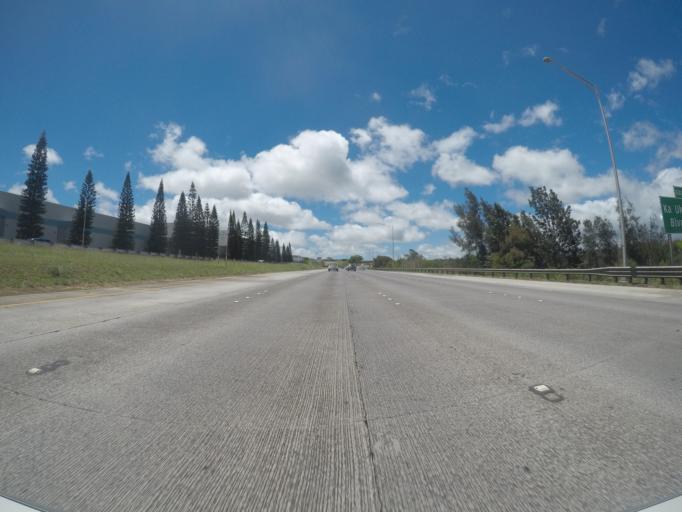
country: US
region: Hawaii
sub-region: Honolulu County
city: Waipio
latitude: 21.4234
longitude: -157.9949
